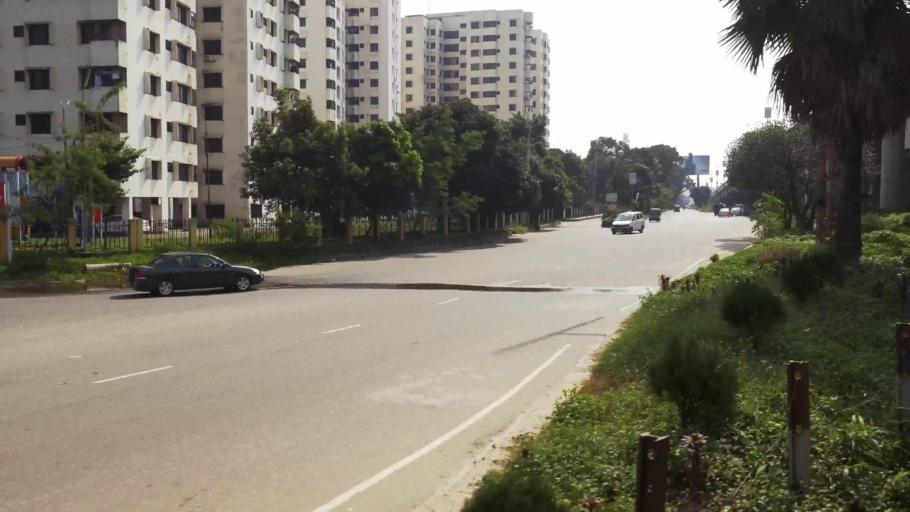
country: BD
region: Dhaka
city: Tungi
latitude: 23.8437
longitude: 90.4152
